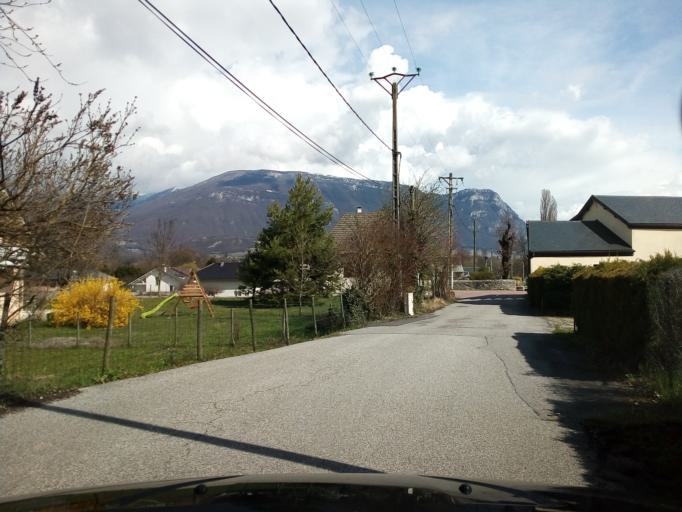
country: FR
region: Rhone-Alpes
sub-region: Departement de la Savoie
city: Saint-Baldoph
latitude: 45.5240
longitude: 5.9528
